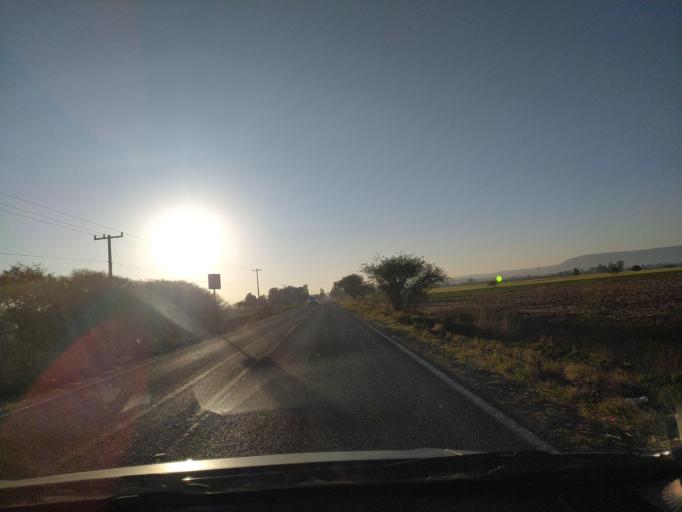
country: MX
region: Guanajuato
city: Ciudad Manuel Doblado
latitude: 20.7449
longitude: -101.8972
